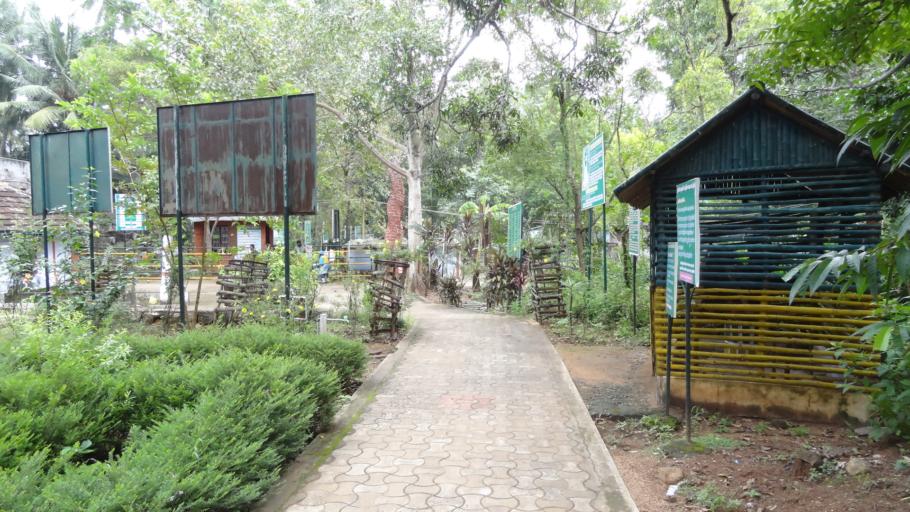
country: IN
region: Tamil Nadu
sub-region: Kanniyakumari
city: Padmanabhapuram
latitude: 8.2421
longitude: 77.3350
